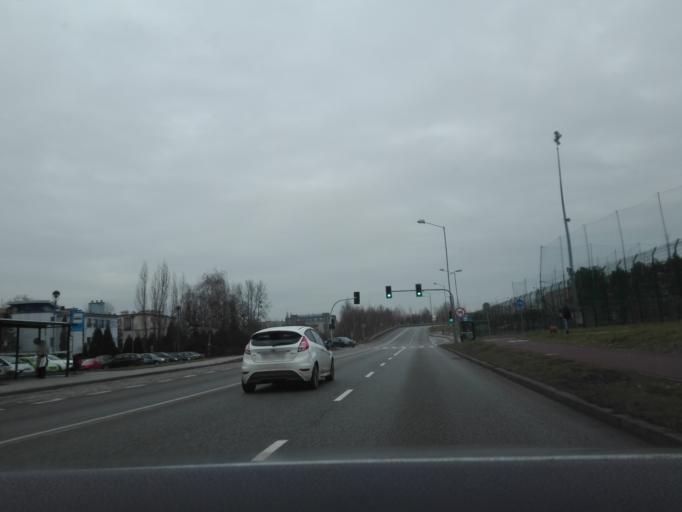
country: PL
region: Silesian Voivodeship
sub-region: Katowice
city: Katowice
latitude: 50.2702
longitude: 19.0154
